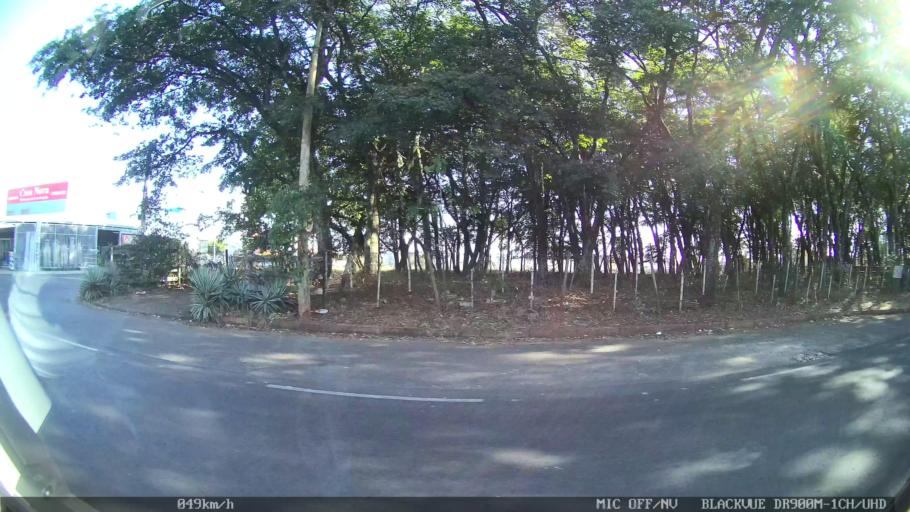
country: BR
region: Sao Paulo
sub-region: Sao Jose Do Rio Preto
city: Sao Jose do Rio Preto
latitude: -20.7655
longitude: -49.3532
